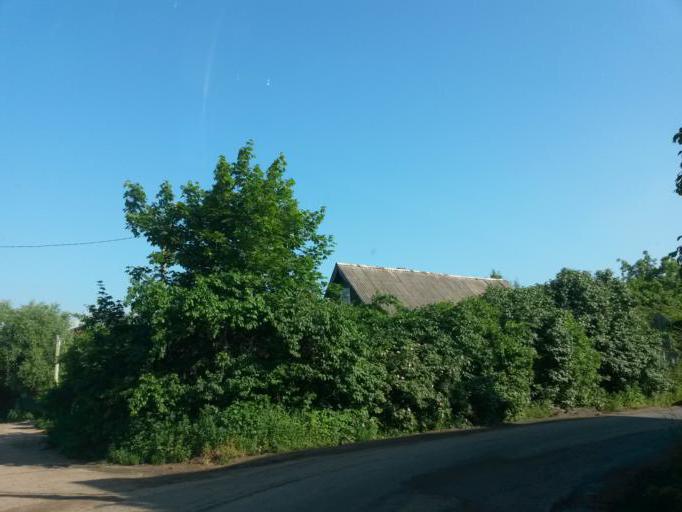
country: RU
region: Moscow
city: Zyablikovo
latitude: 55.5880
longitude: 37.7836
